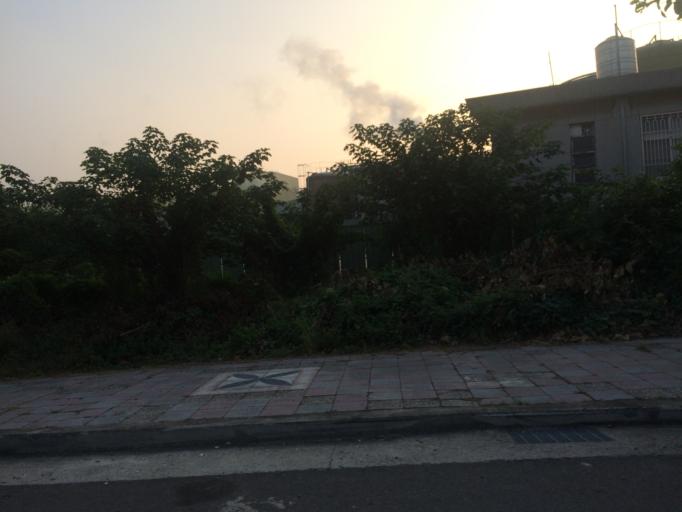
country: TW
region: Taiwan
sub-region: Hsinchu
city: Hsinchu
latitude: 24.7314
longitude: 120.9155
